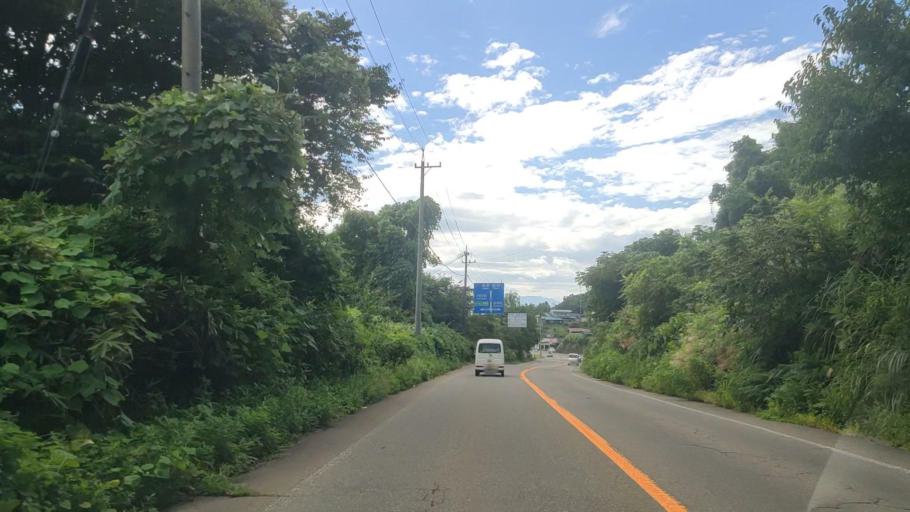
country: JP
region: Nagano
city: Nakano
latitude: 36.7581
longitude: 138.3175
